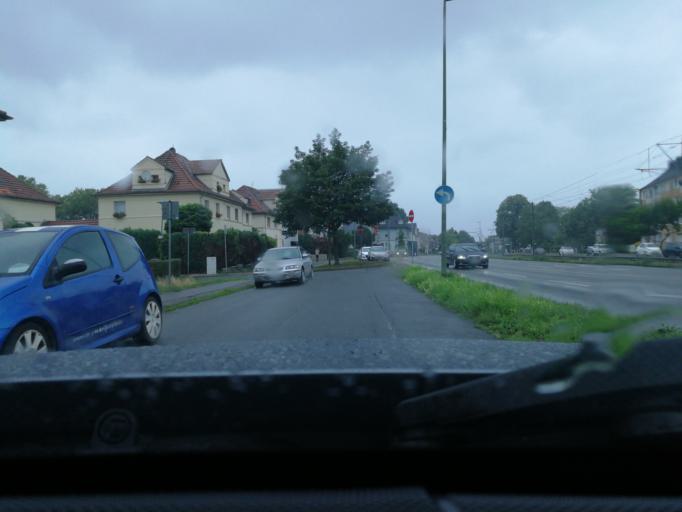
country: DE
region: North Rhine-Westphalia
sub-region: Regierungsbezirk Dusseldorf
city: Dinslaken
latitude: 51.5365
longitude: 6.7396
